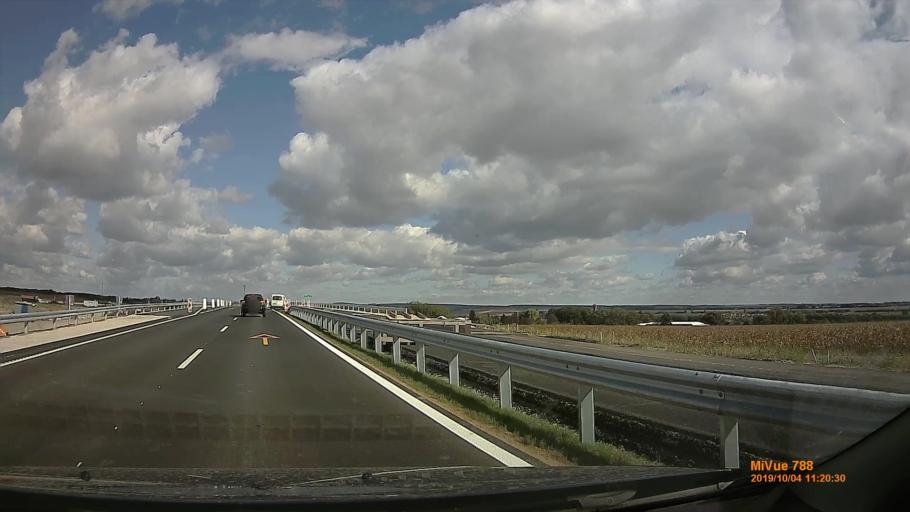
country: HU
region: Somogy
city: Kaposvar
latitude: 46.4979
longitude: 17.8098
